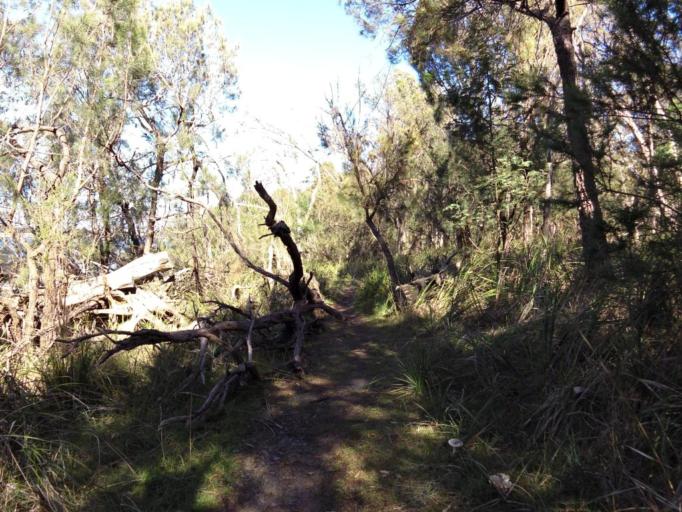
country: AU
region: Victoria
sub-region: Casey
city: Narre Warren North
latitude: -37.9639
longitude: 145.2942
